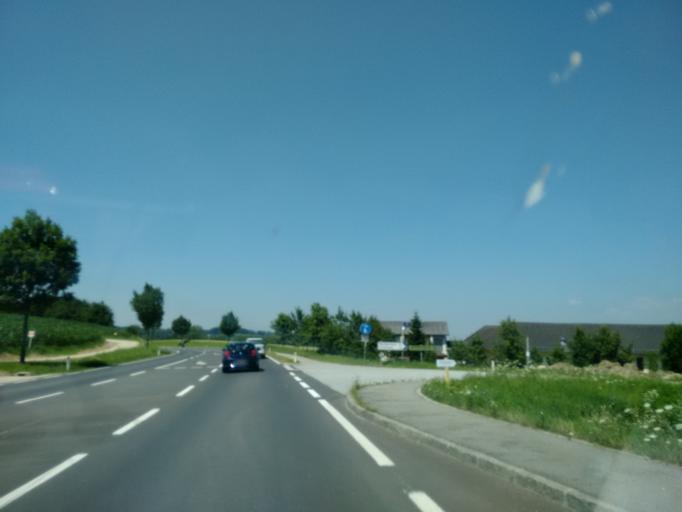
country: AT
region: Upper Austria
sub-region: Politischer Bezirk Grieskirchen
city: Bad Schallerbach
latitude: 48.2317
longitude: 13.9666
